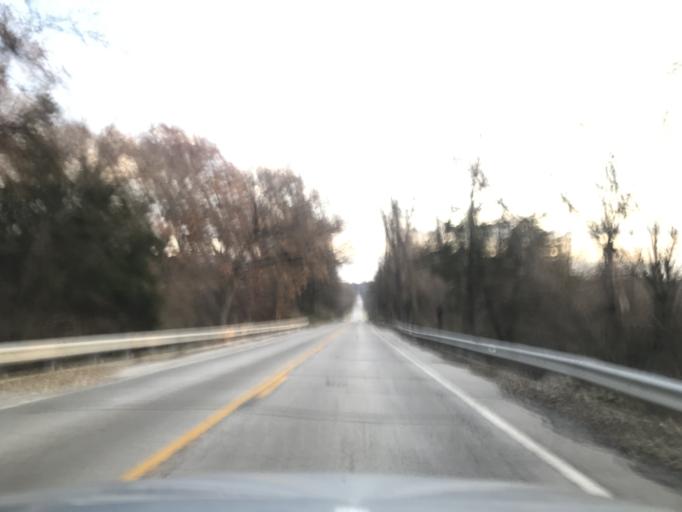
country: US
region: Illinois
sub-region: Henderson County
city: Oquawka
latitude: 40.9123
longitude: -90.8643
